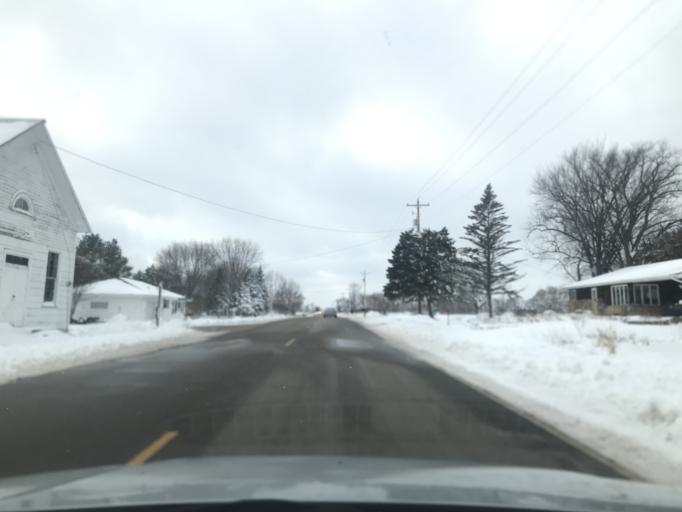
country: US
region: Wisconsin
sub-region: Oconto County
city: Oconto
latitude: 44.9499
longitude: -87.9053
